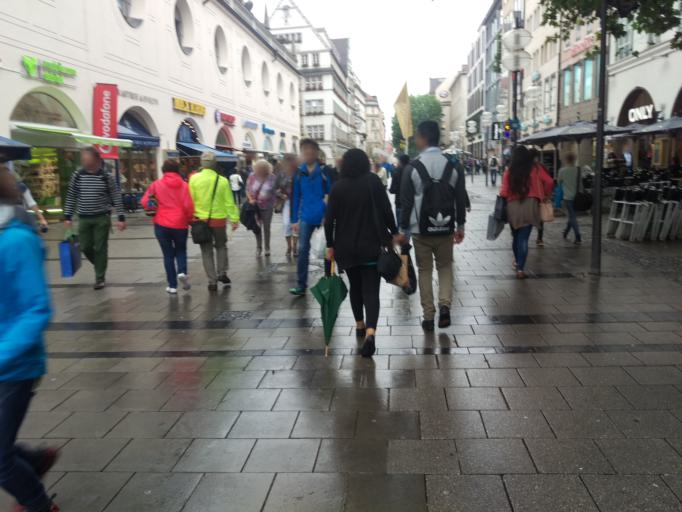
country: DE
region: Bavaria
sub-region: Upper Bavaria
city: Munich
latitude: 48.1385
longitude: 11.5705
